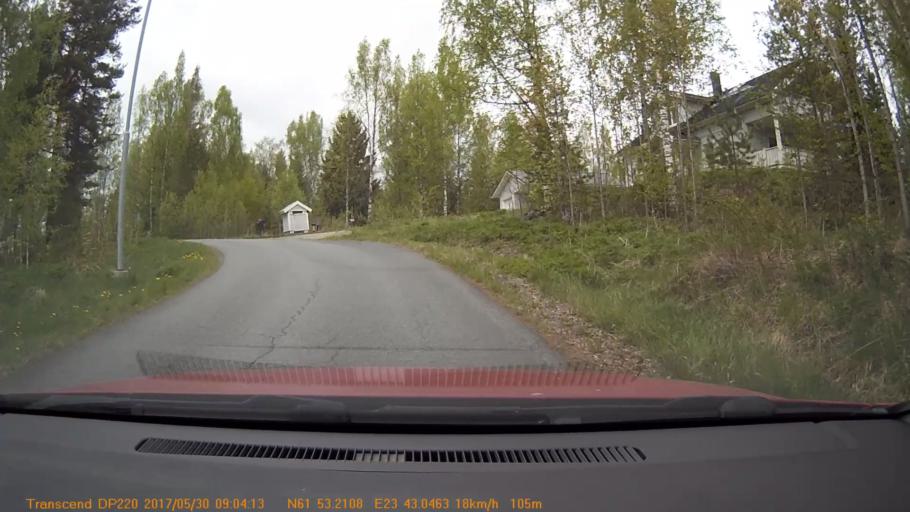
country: FI
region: Pirkanmaa
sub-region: Tampere
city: Kuru
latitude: 61.8867
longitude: 23.7175
